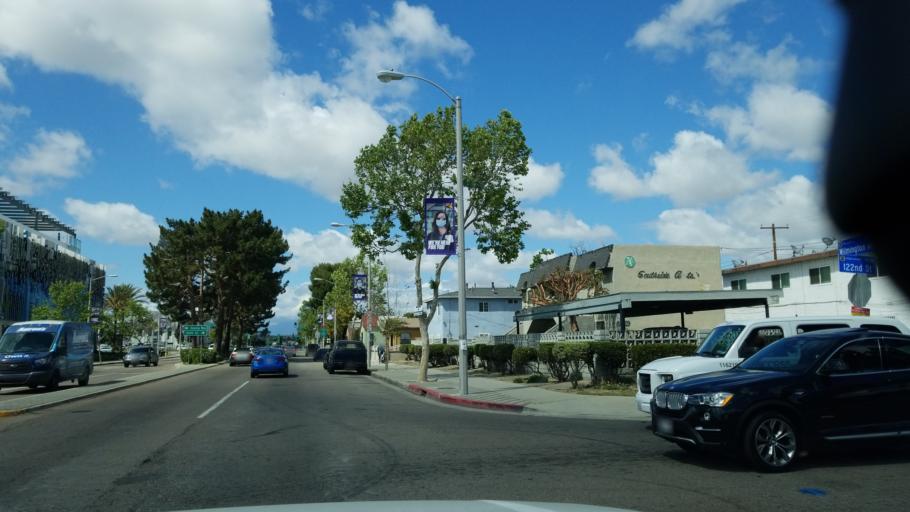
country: US
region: California
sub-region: Los Angeles County
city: Willowbrook
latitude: 33.9218
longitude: -118.2388
